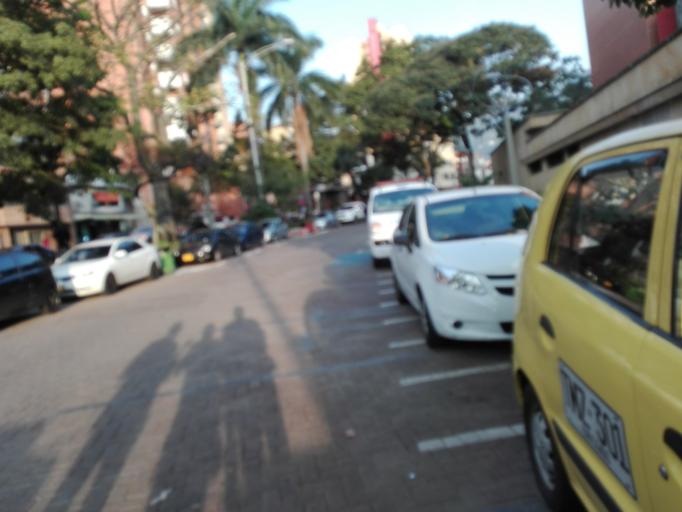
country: CO
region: Antioquia
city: Medellin
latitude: 6.2478
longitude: -75.5592
